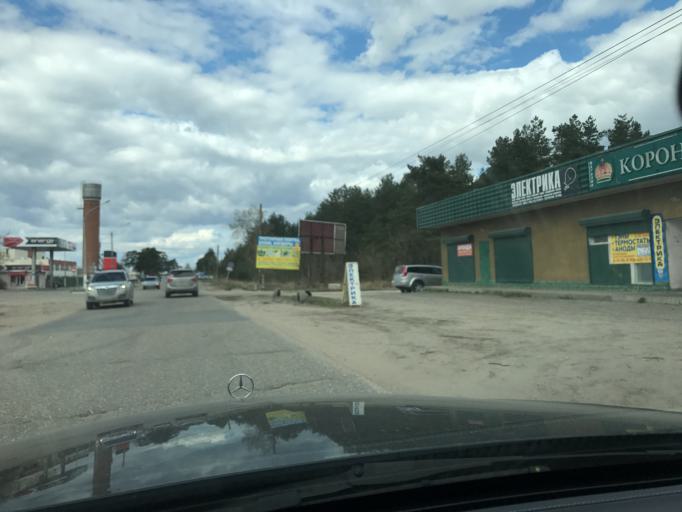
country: RU
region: Vladimir
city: Pokrov
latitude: 55.9010
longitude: 39.1970
